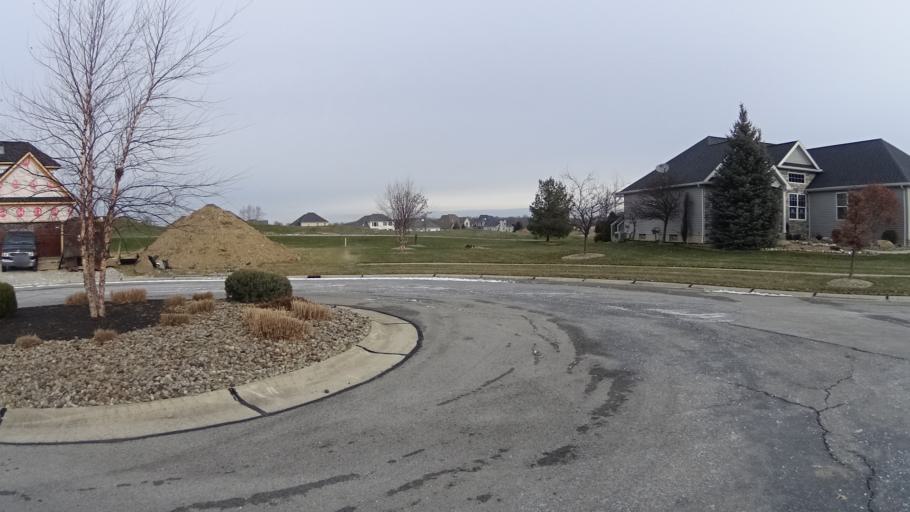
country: US
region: Ohio
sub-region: Lorain County
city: Lagrange
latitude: 41.2452
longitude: -82.1129
